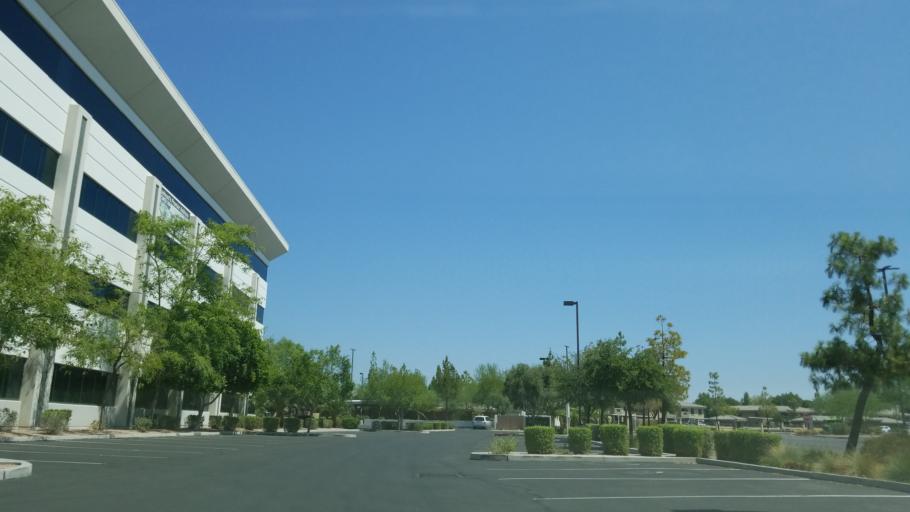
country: US
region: Arizona
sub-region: Maricopa County
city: Sun City
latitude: 33.6438
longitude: -112.2290
